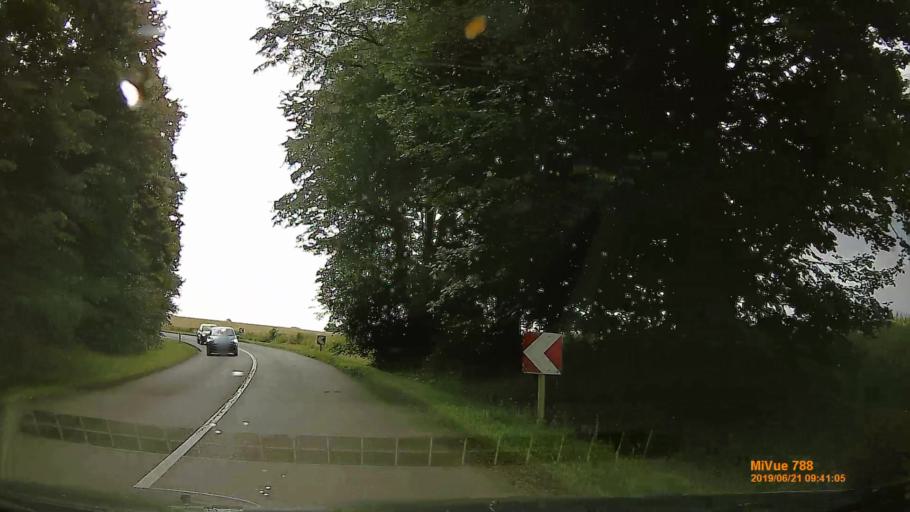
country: HU
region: Somogy
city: Taszar
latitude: 46.2919
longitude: 17.9521
